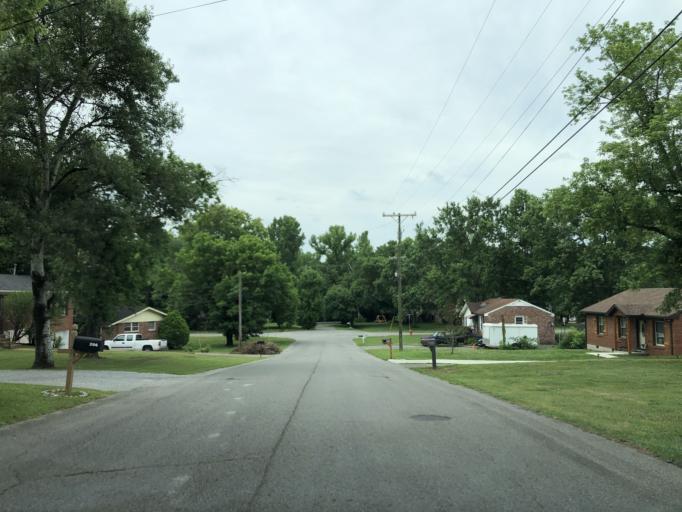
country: US
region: Tennessee
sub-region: Davidson County
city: Goodlettsville
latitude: 36.2864
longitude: -86.7106
